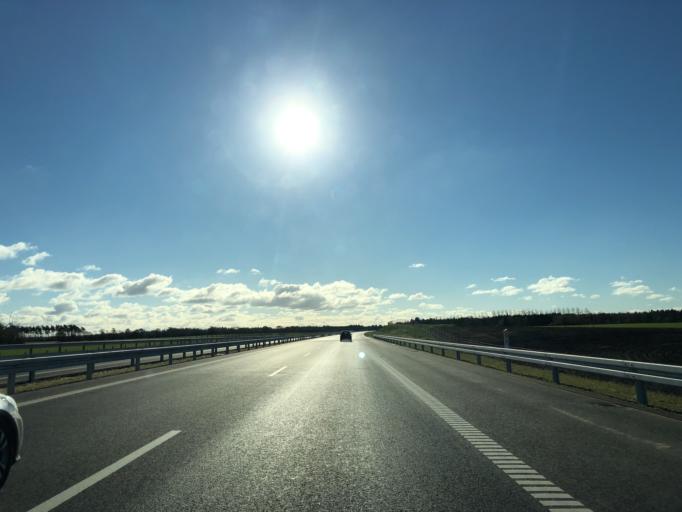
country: DK
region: Central Jutland
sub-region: Herning Kommune
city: Avlum
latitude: 56.3468
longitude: 8.7376
